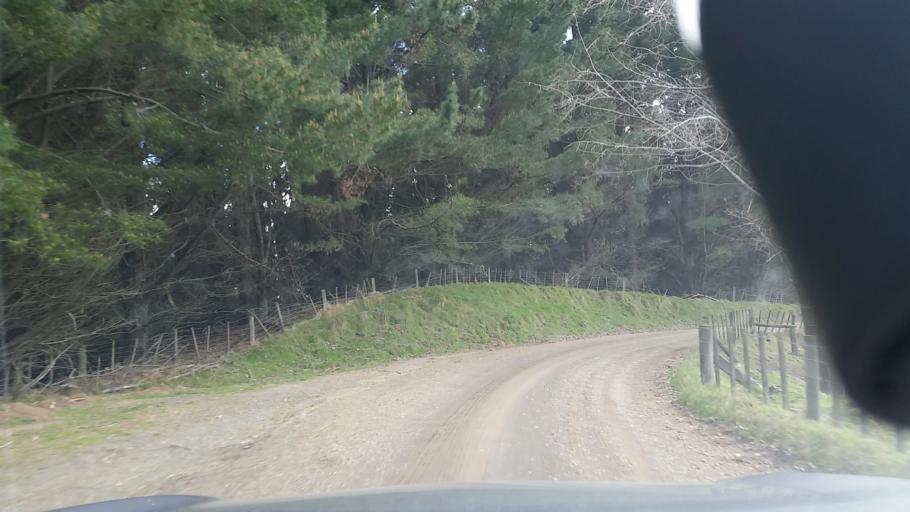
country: NZ
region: Hawke's Bay
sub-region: Napier City
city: Napier
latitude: -39.2285
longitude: 176.9834
